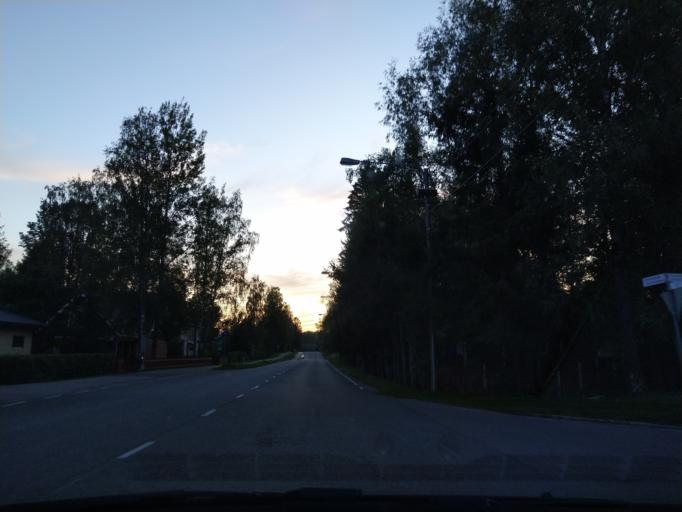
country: FI
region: Uusimaa
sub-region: Helsinki
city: Tuusula
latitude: 60.3545
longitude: 25.0493
